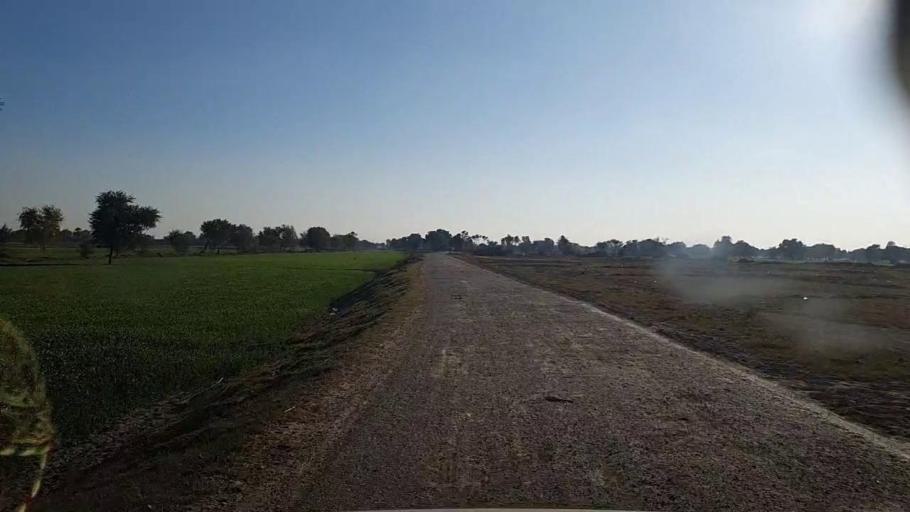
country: PK
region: Sindh
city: Khairpur
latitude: 28.0070
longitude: 69.7204
